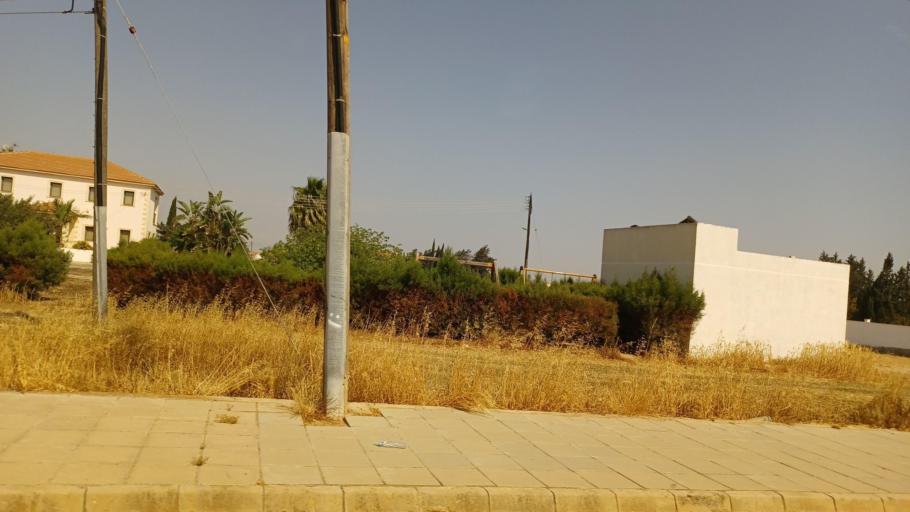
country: CY
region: Ammochostos
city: Avgorou
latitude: 35.0370
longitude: 33.8457
